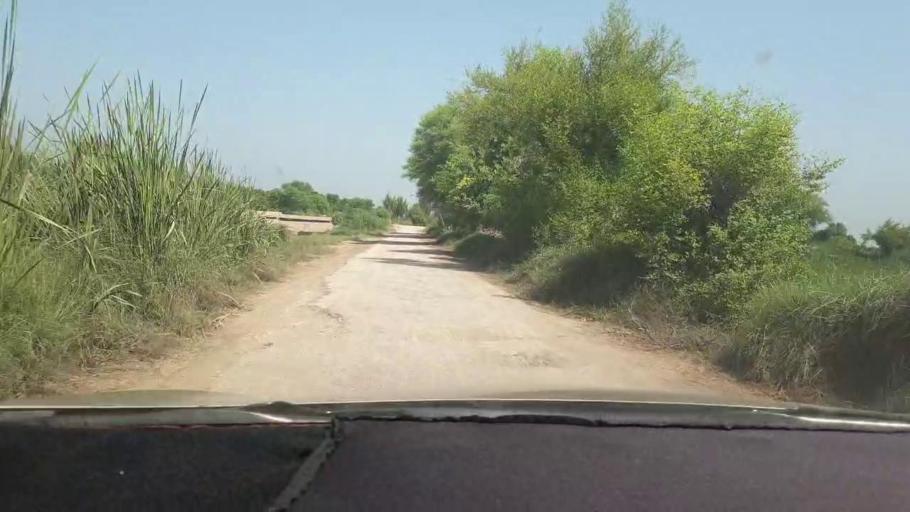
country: PK
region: Sindh
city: Miro Khan
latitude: 27.7029
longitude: 68.0864
